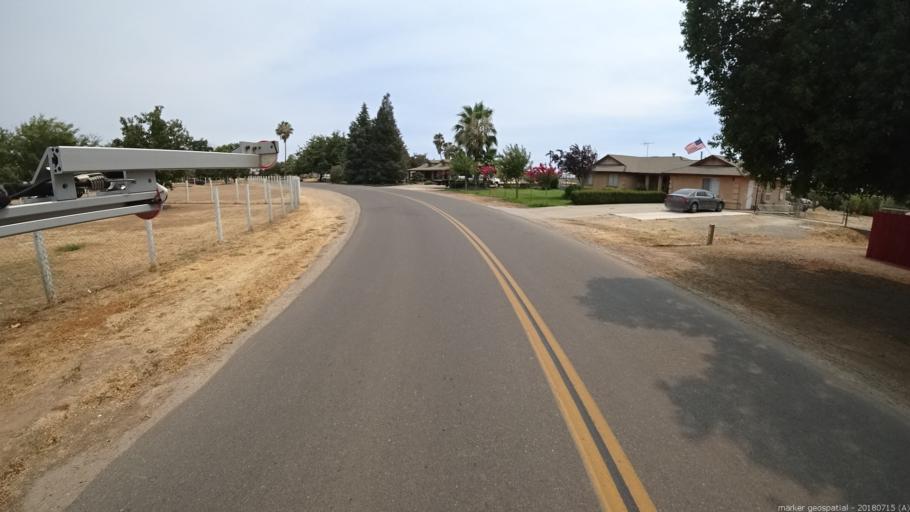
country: US
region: California
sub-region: Madera County
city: Madera Acres
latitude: 37.0046
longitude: -120.1049
